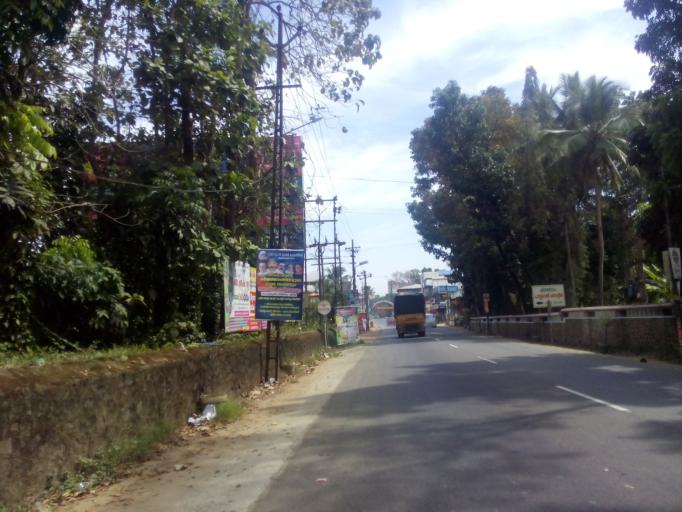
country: IN
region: Kerala
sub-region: Kottayam
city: Lalam
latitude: 9.7092
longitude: 76.6751
